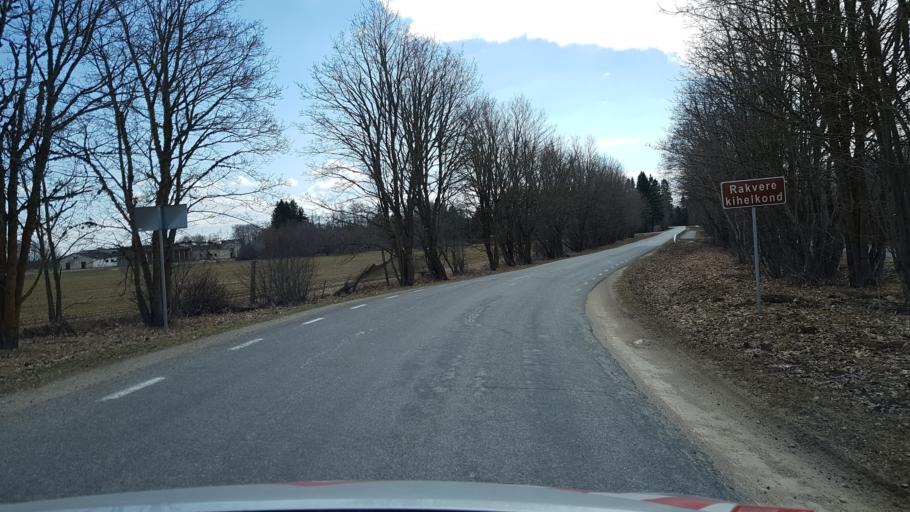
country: EE
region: Laeaene-Virumaa
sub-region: Haljala vald
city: Haljala
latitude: 59.3950
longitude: 26.2888
